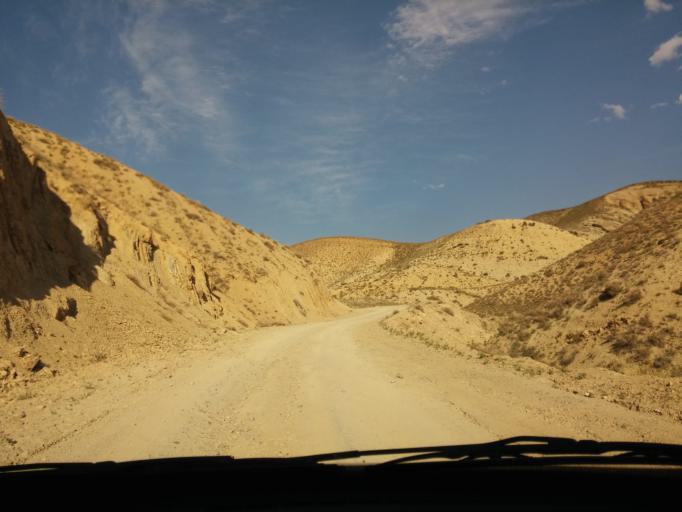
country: IR
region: Tehran
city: Damavand
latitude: 35.5348
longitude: 52.2012
